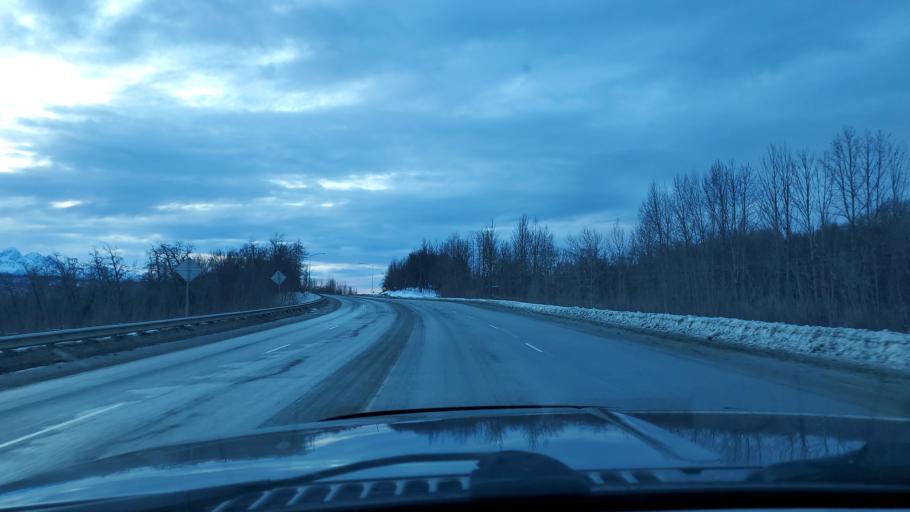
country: US
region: Alaska
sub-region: Matanuska-Susitna Borough
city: Lazy Mountain
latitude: 61.6943
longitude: -148.9655
